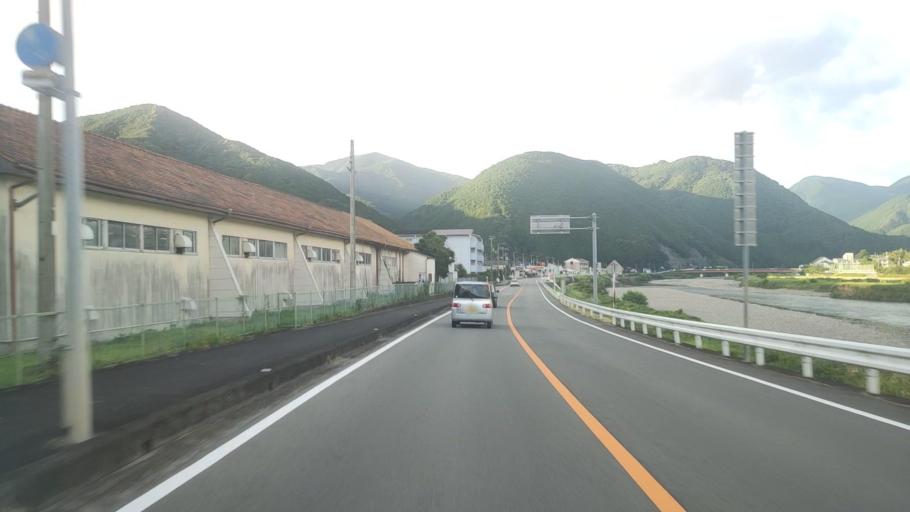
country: JP
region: Wakayama
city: Tanabe
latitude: 33.7249
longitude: 135.4817
